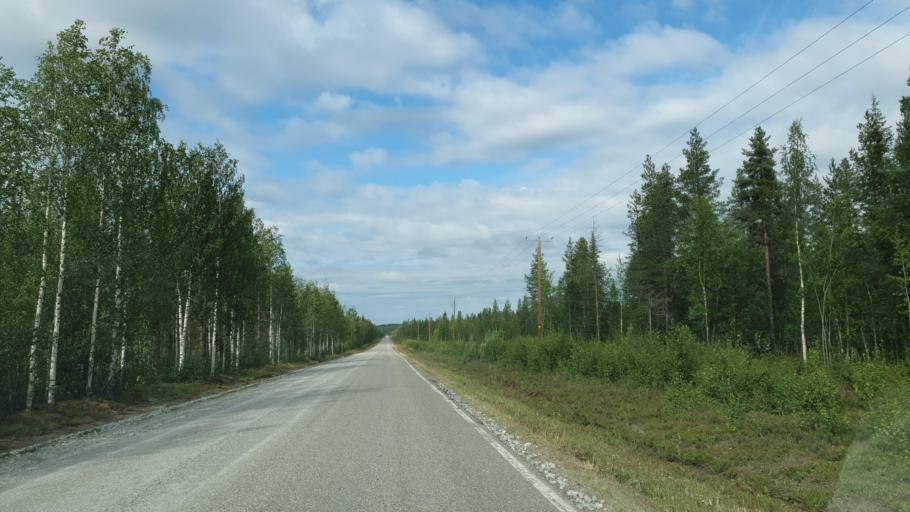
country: FI
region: Lapland
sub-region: Pohjois-Lappi
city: Sodankylae
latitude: 67.5378
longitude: 25.9565
